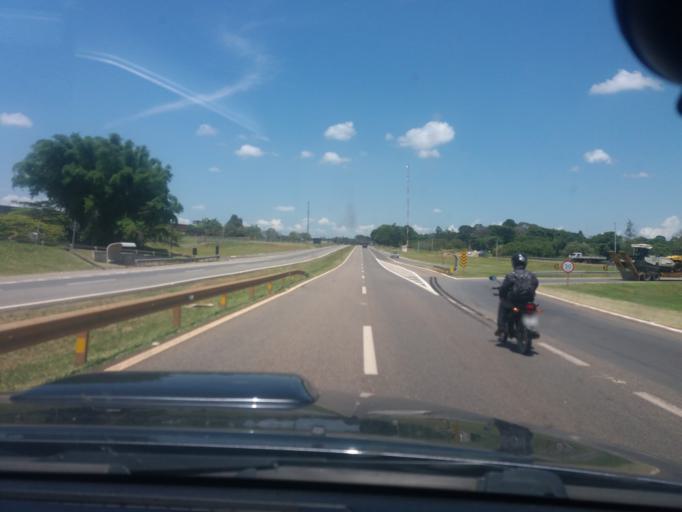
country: BR
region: Sao Paulo
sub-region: Tatui
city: Tatui
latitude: -23.3598
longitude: -47.8884
